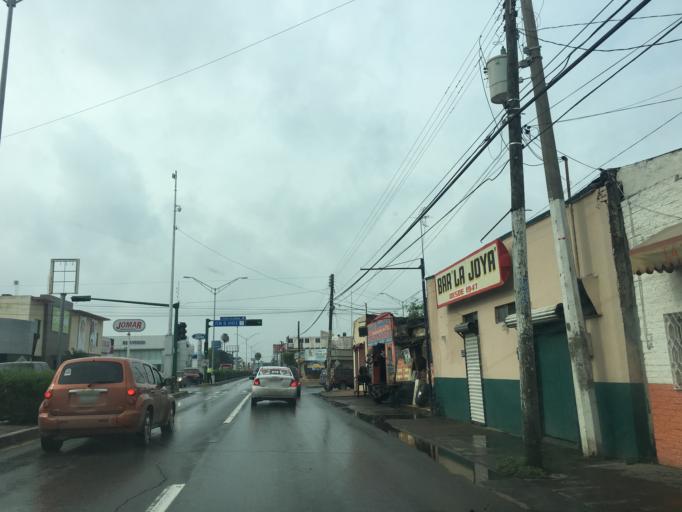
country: MX
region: Tamaulipas
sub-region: Matamoros
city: Heroica Matamoros
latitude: 25.8672
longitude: -97.5039
